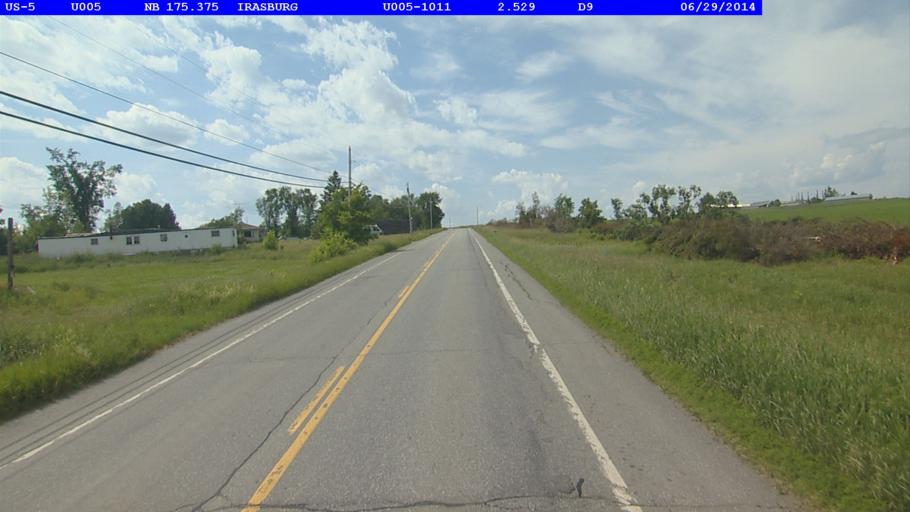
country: US
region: Vermont
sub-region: Orleans County
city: Newport
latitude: 44.8324
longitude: -72.2479
